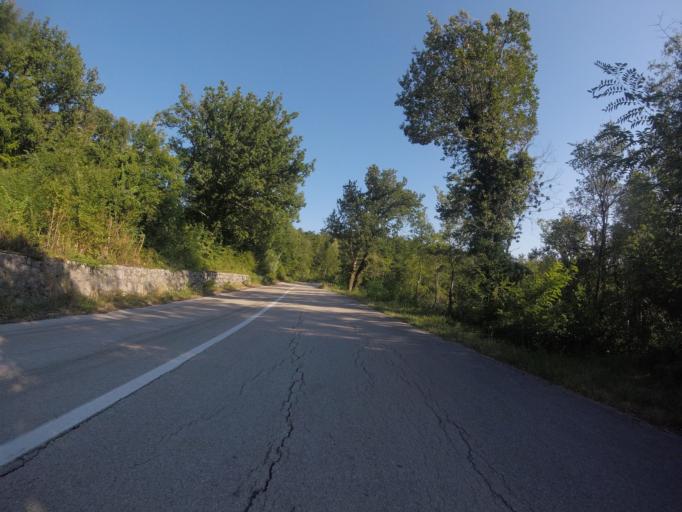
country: HR
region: Primorsko-Goranska
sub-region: Grad Crikvenica
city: Crikvenica
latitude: 45.2186
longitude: 14.6942
